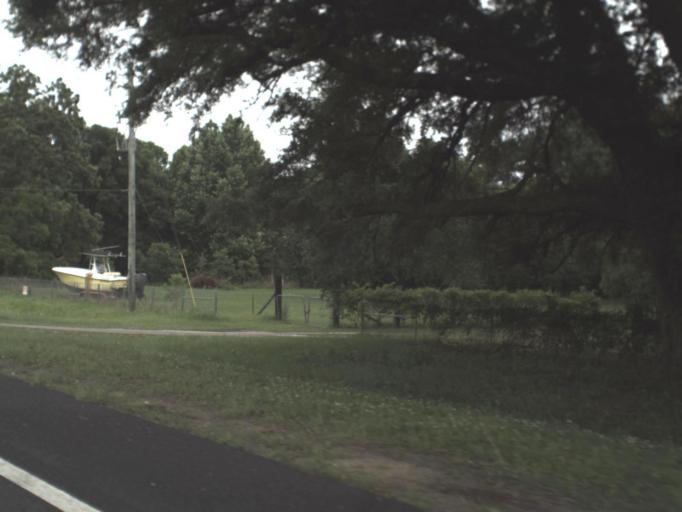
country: US
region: Florida
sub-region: Nassau County
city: Yulee
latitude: 30.6163
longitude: -81.7131
